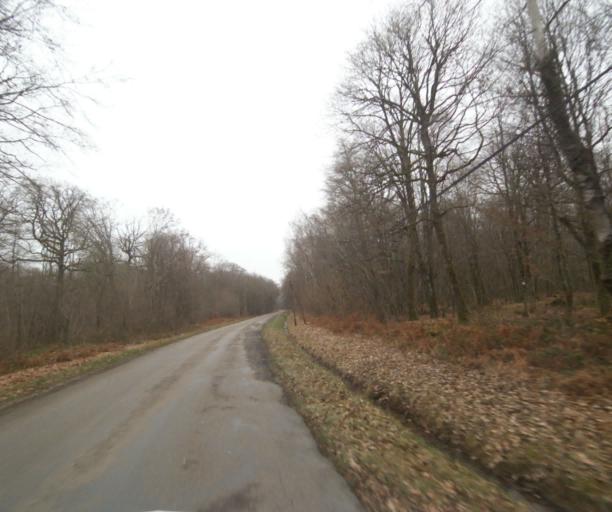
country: FR
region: Champagne-Ardenne
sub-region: Departement de la Haute-Marne
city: Wassy
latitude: 48.5267
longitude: 4.9764
